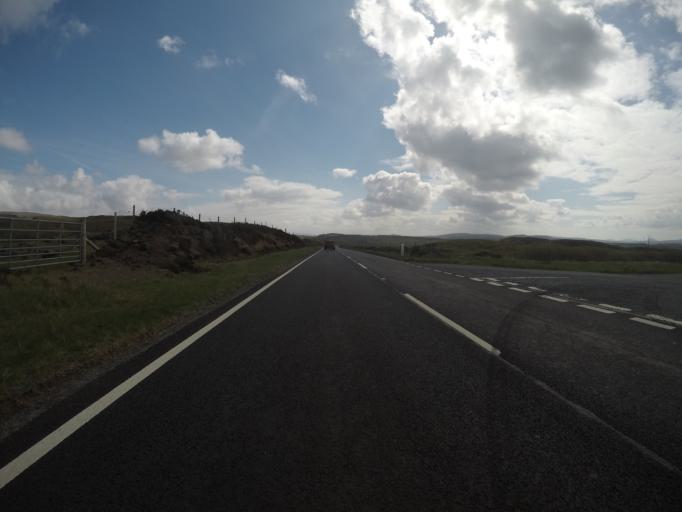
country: GB
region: Scotland
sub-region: Highland
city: Portree
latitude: 57.5387
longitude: -6.3625
